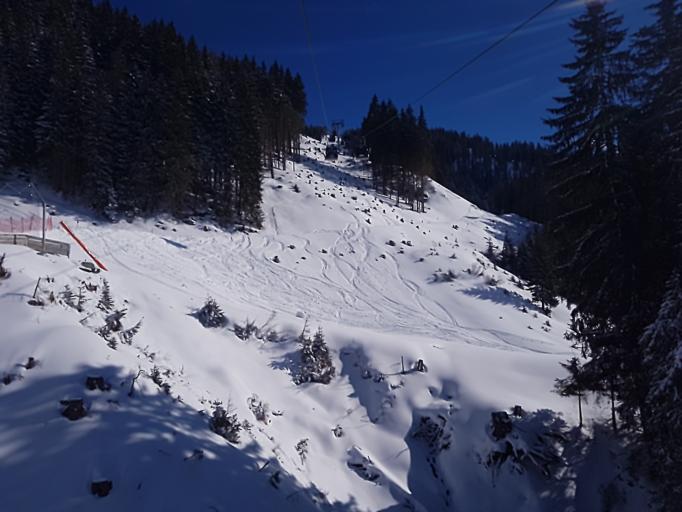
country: AT
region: Salzburg
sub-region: Politischer Bezirk Zell am See
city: Saalbach
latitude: 47.4097
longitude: 12.5855
